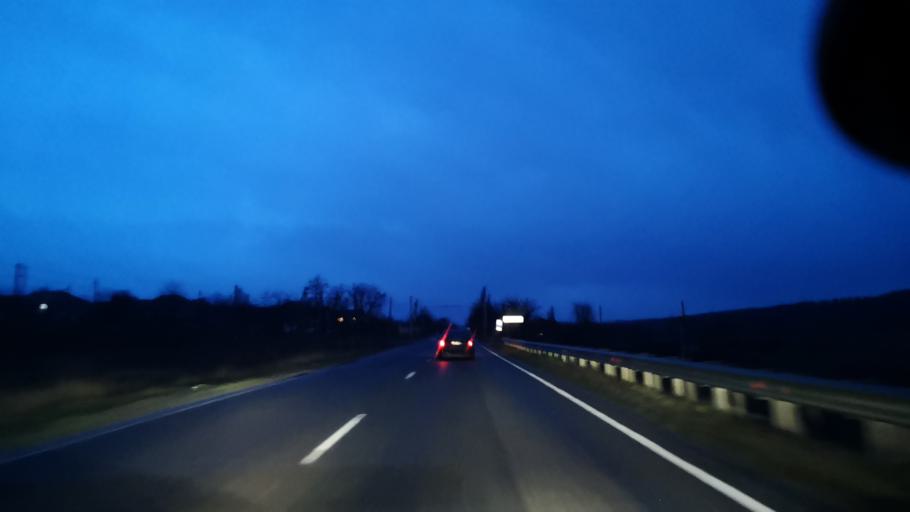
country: MD
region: Orhei
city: Orhei
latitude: 47.4203
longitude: 28.8075
